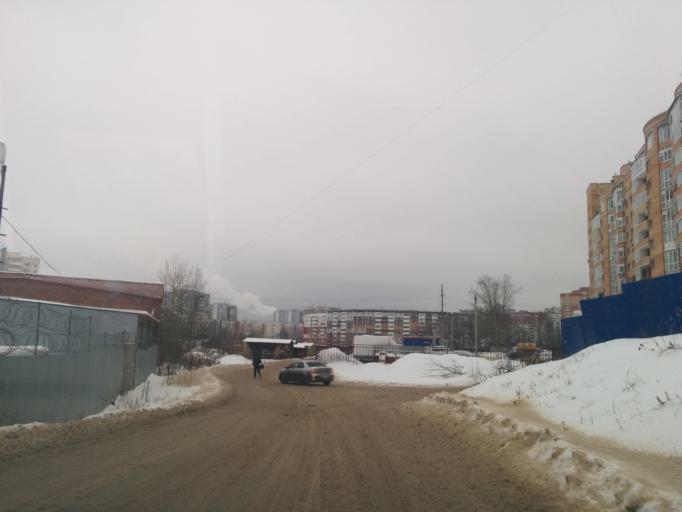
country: RU
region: Perm
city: Perm
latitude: 58.0151
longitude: 56.3037
